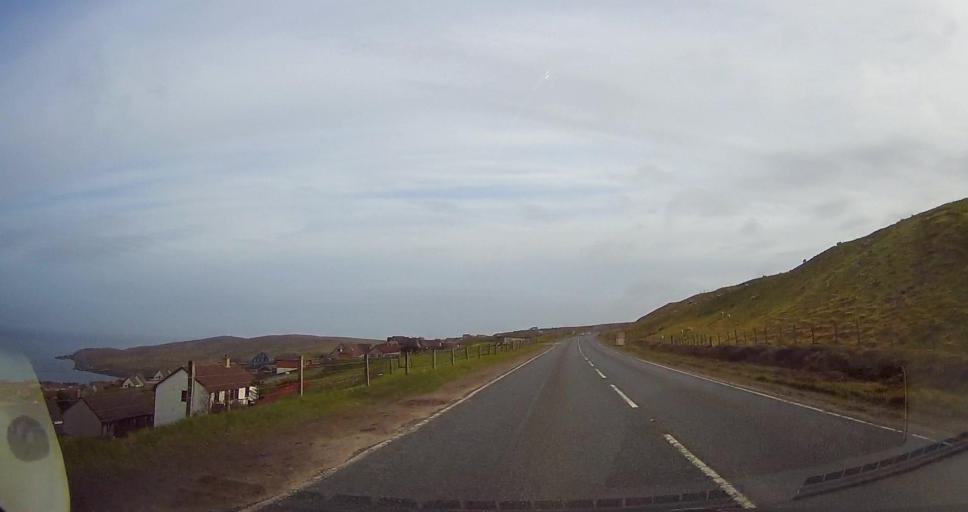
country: GB
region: Scotland
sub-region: Shetland Islands
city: Lerwick
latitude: 60.1316
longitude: -1.2148
